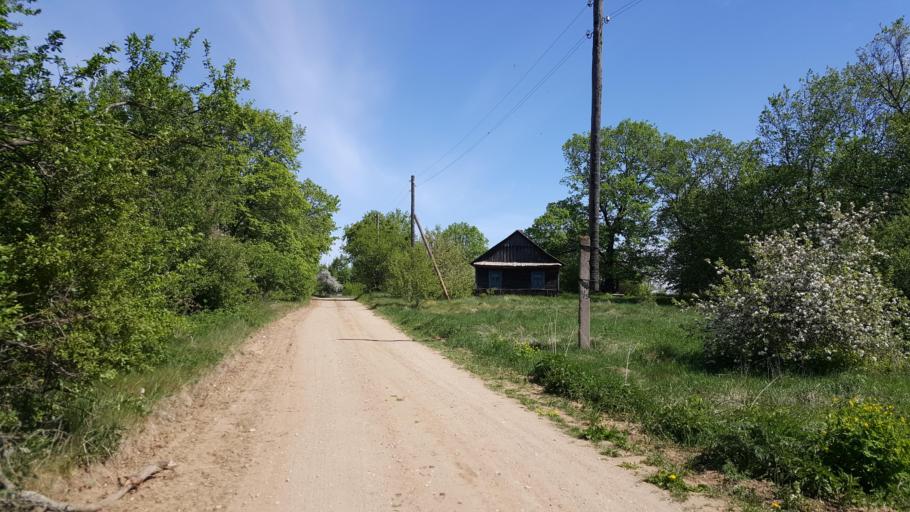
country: BY
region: Brest
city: Zhabinka
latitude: 52.3830
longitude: 24.0225
